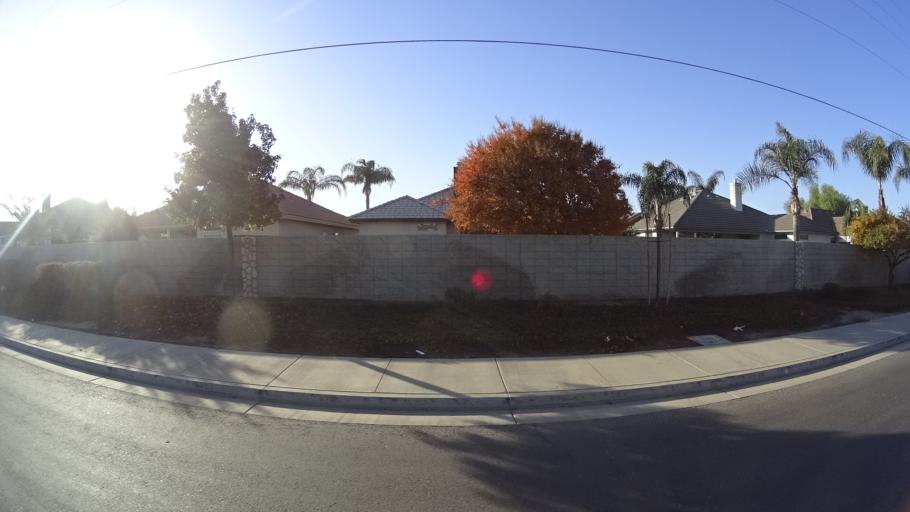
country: US
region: California
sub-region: Kern County
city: Greenfield
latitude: 35.2742
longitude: -119.0485
